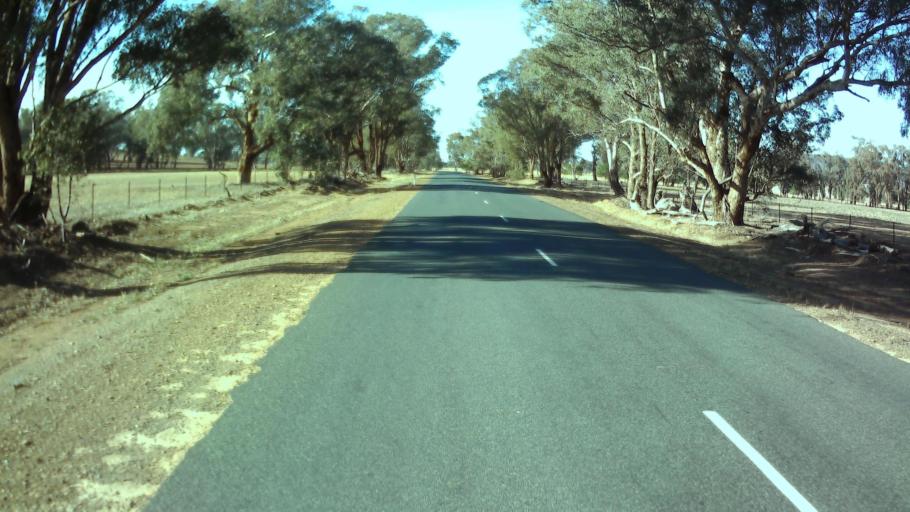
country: AU
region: New South Wales
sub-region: Weddin
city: Grenfell
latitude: -33.9399
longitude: 148.1368
